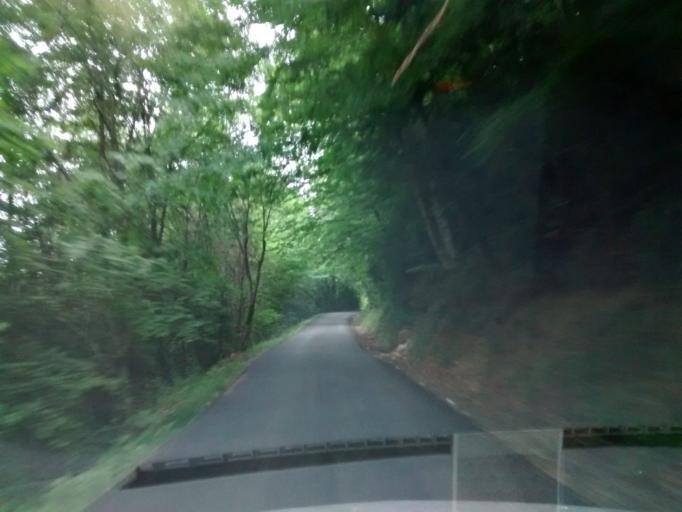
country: ES
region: Aragon
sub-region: Provincia de Huesca
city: Puertolas
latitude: 42.5848
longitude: 0.1381
